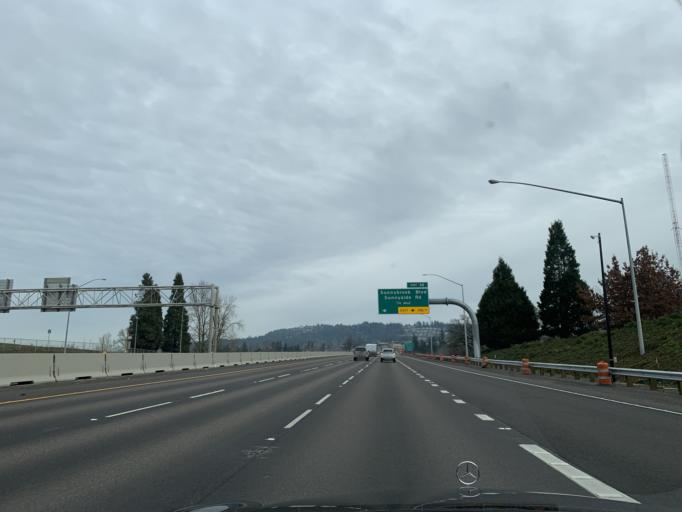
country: US
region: Oregon
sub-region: Clackamas County
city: Clackamas
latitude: 45.4204
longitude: -122.5724
